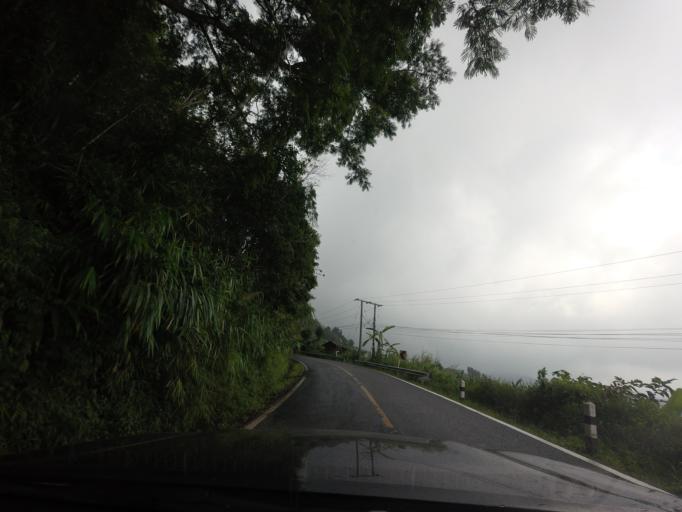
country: TH
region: Nan
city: Bo Kluea
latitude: 19.1817
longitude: 101.0798
